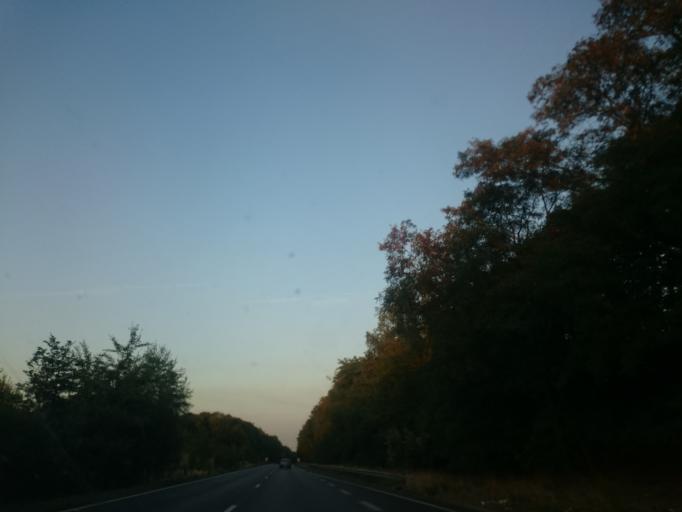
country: FR
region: Ile-de-France
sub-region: Departement de l'Essonne
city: Bondoufle
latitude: 48.6239
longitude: 2.3760
